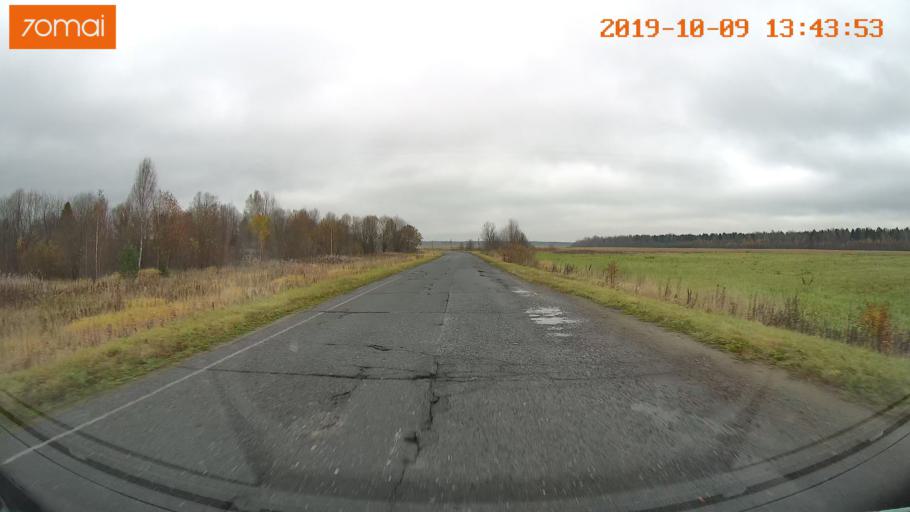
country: RU
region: Kostroma
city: Buy
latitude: 58.3612
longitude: 41.2050
